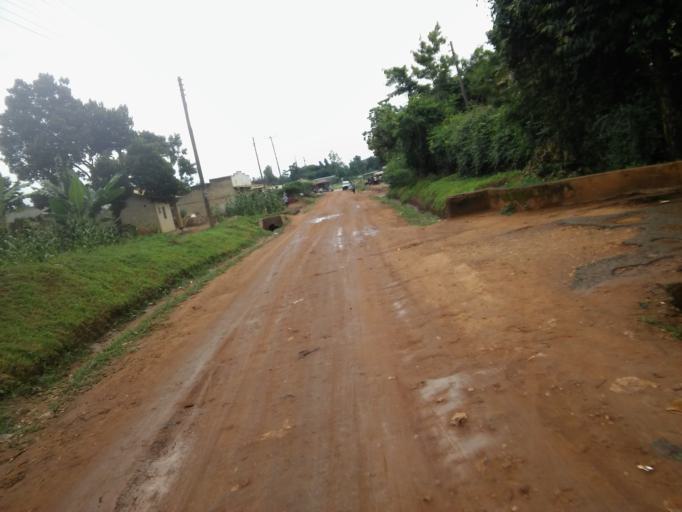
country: UG
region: Eastern Region
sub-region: Mbale District
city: Mbale
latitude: 1.0400
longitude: 34.1795
